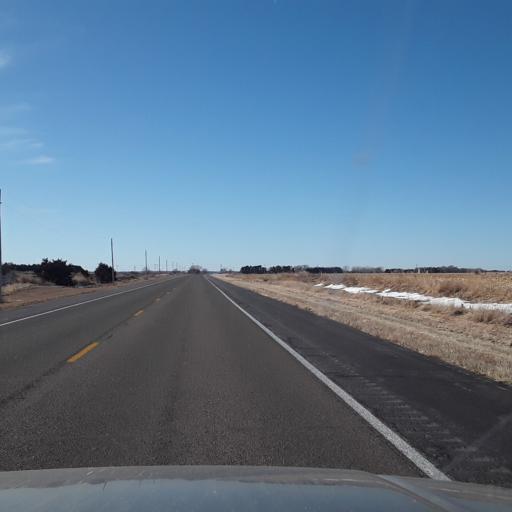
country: US
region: Nebraska
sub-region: Kearney County
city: Minden
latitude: 40.5432
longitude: -98.8491
